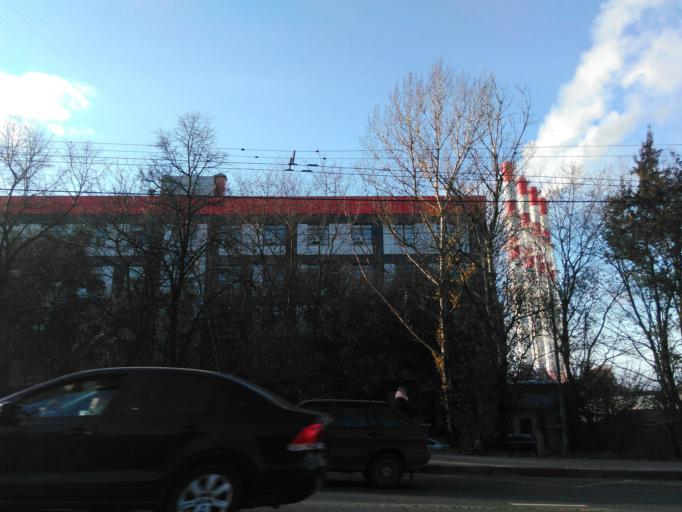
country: RU
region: Moscow
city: Mar'ina Roshcha
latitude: 55.8107
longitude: 37.6184
